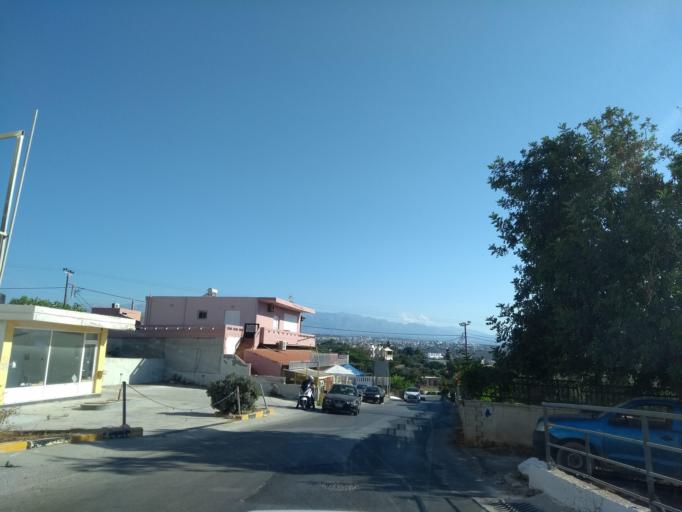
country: GR
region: Crete
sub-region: Nomos Chanias
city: Pithari
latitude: 35.5617
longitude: 24.0926
